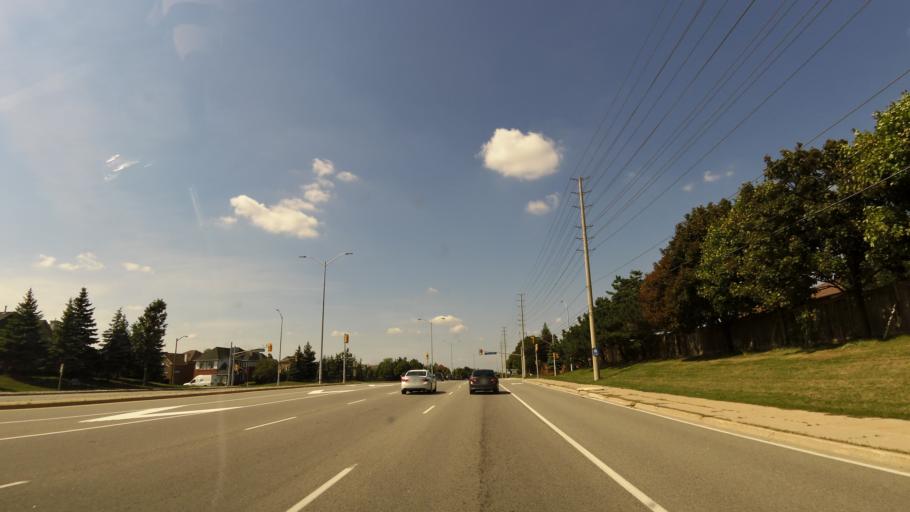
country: CA
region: Ontario
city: Mississauga
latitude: 43.5727
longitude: -79.7266
